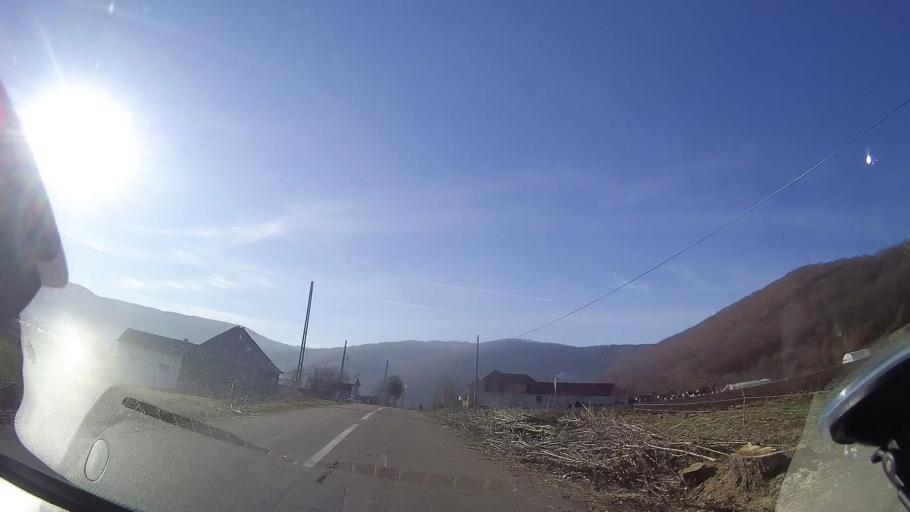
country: RO
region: Bihor
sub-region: Comuna Suncuius
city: Suncuius
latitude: 46.9576
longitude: 22.5396
